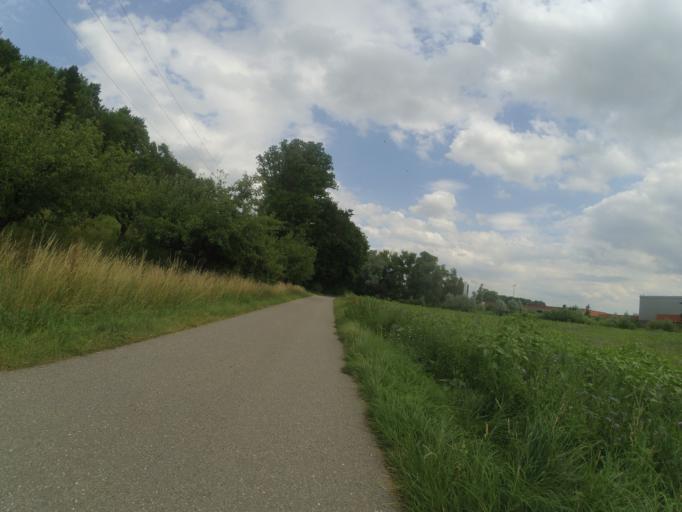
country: DE
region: Baden-Wuerttemberg
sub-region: Tuebingen Region
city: Ehingen
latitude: 48.2738
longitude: 9.7258
